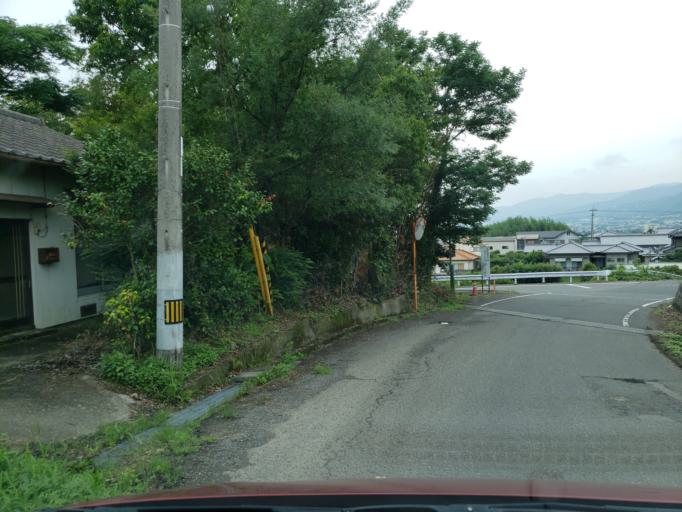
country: JP
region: Tokushima
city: Kamojimacho-jogejima
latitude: 34.0988
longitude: 134.2834
